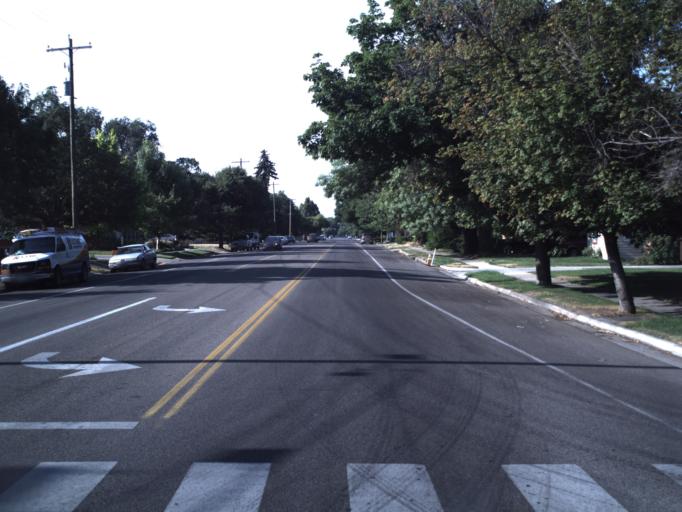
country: US
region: Utah
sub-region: Utah County
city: American Fork
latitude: 40.3830
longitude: -111.7959
